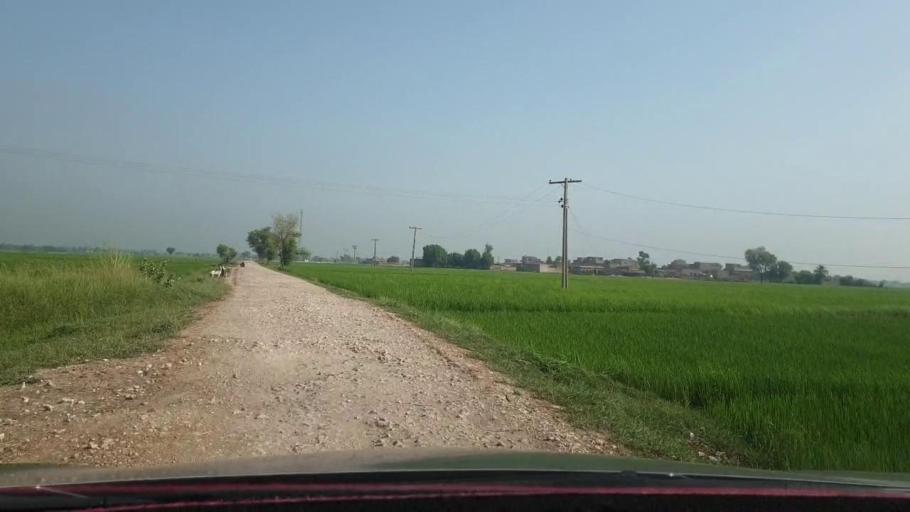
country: PK
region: Sindh
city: Nasirabad
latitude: 27.4808
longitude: 67.9257
